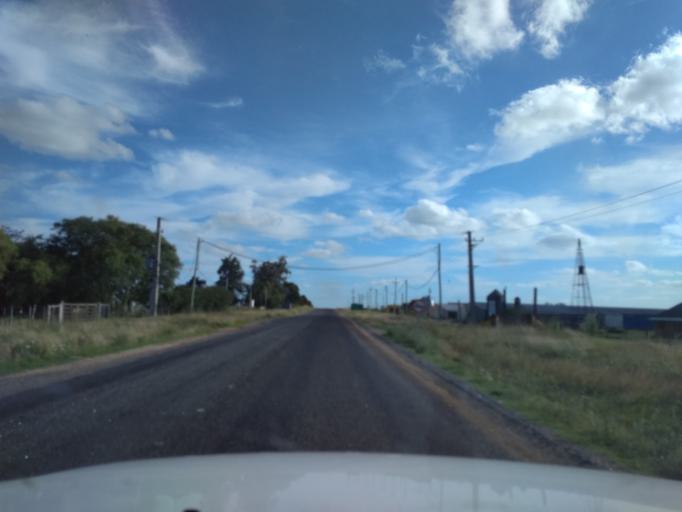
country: UY
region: Canelones
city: San Ramon
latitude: -34.2477
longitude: -55.9258
